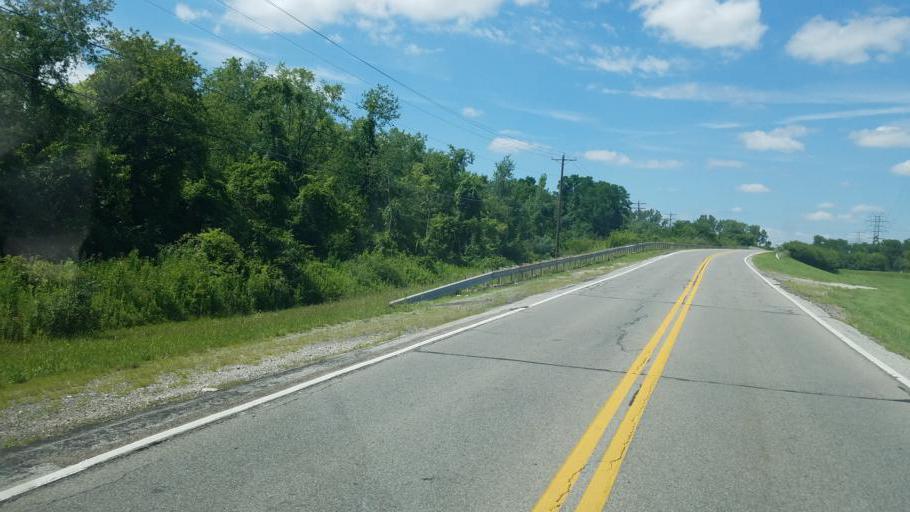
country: US
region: Ohio
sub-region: Franklin County
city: Obetz
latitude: 39.8712
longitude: -82.9886
